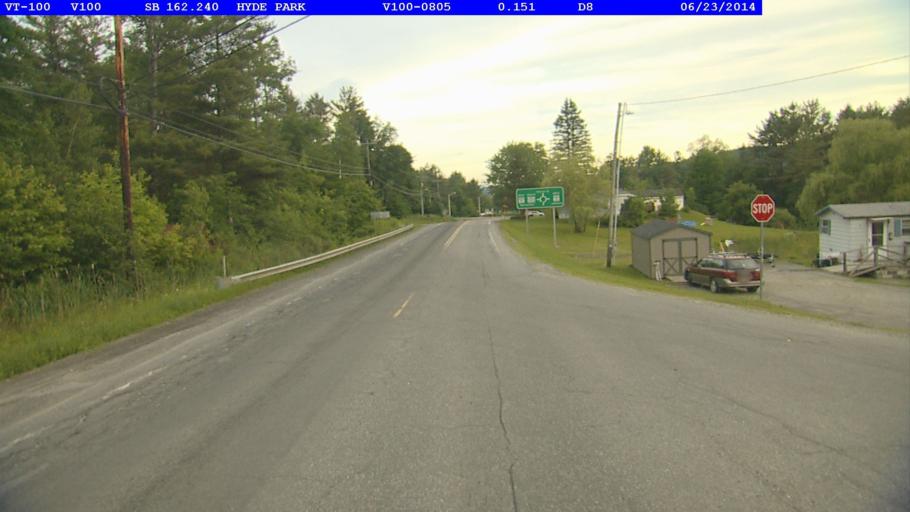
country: US
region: Vermont
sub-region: Lamoille County
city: Hyde Park
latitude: 44.5991
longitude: -72.6156
